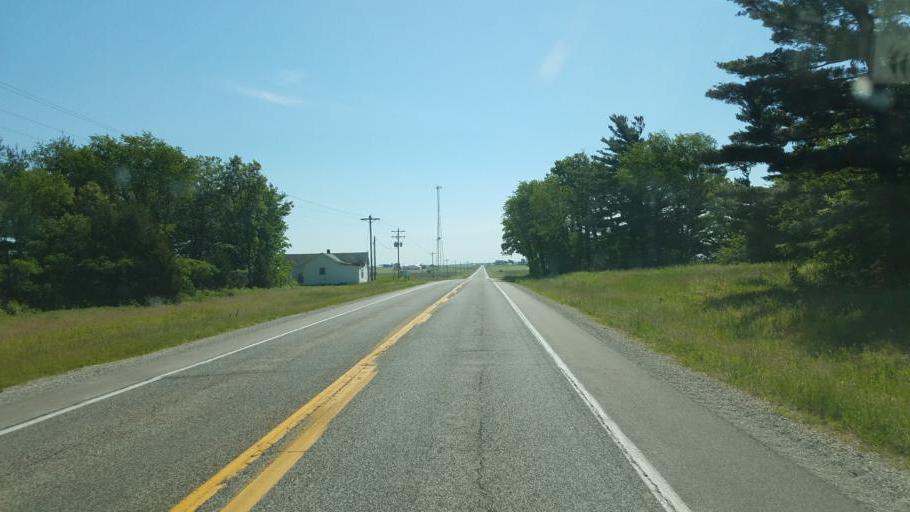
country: US
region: Illinois
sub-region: Mason County
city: Manito
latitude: 40.3036
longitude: -89.7794
